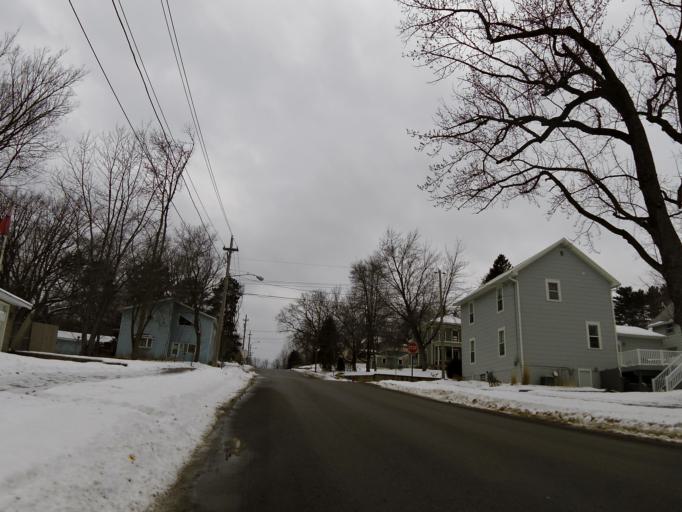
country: US
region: Minnesota
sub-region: Washington County
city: Stillwater
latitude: 45.0649
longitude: -92.8097
